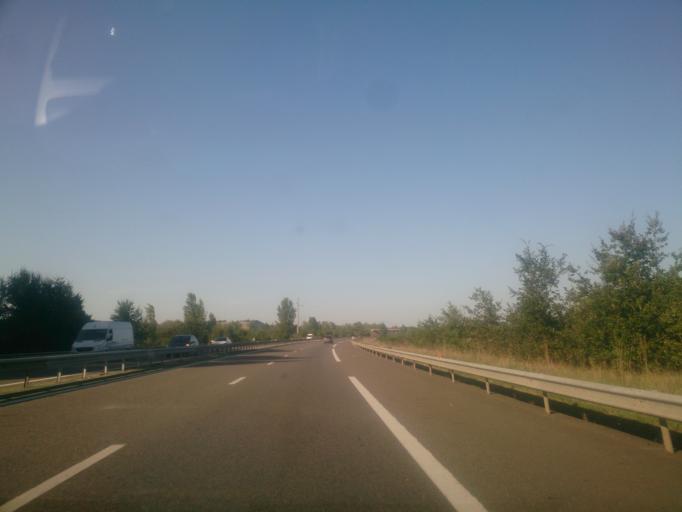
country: FR
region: Midi-Pyrenees
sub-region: Departement du Tarn-et-Garonne
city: Albias
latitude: 44.0874
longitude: 1.4225
